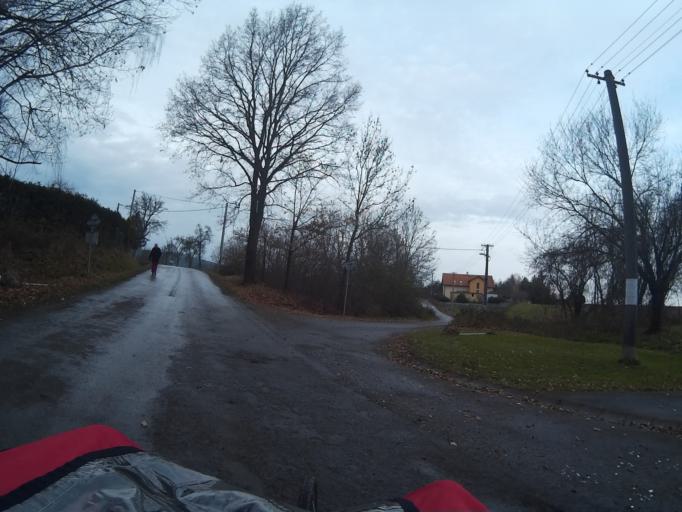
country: CZ
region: Plzensky
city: St'ahlavy
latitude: 49.6736
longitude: 13.4957
